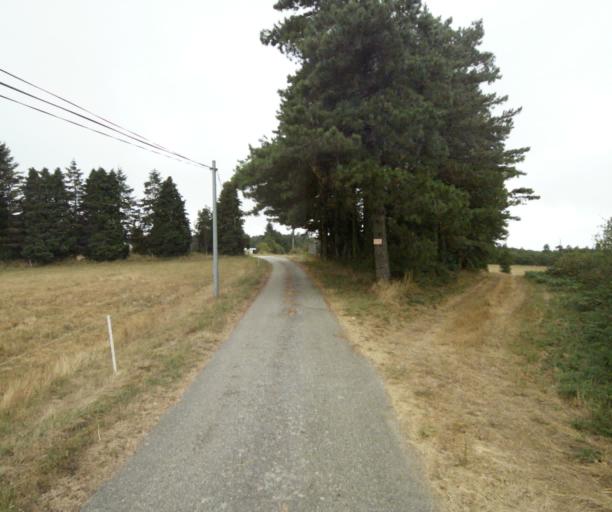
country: FR
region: Midi-Pyrenees
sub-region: Departement du Tarn
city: Soreze
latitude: 43.4144
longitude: 2.0437
